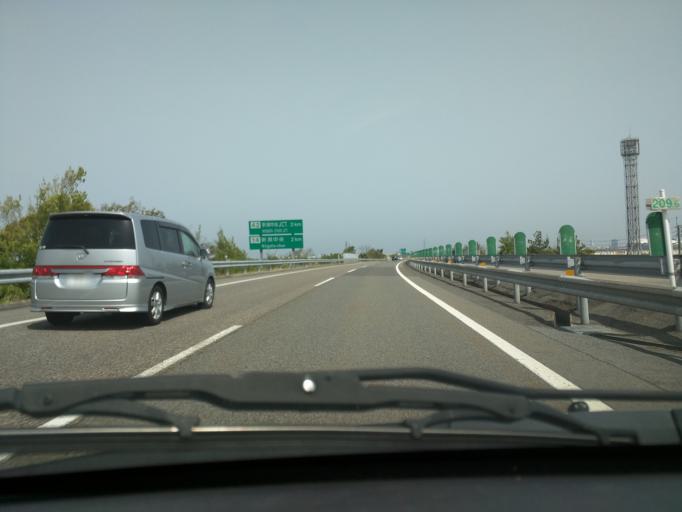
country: JP
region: Niigata
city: Niigata-shi
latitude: 37.8540
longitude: 139.0536
